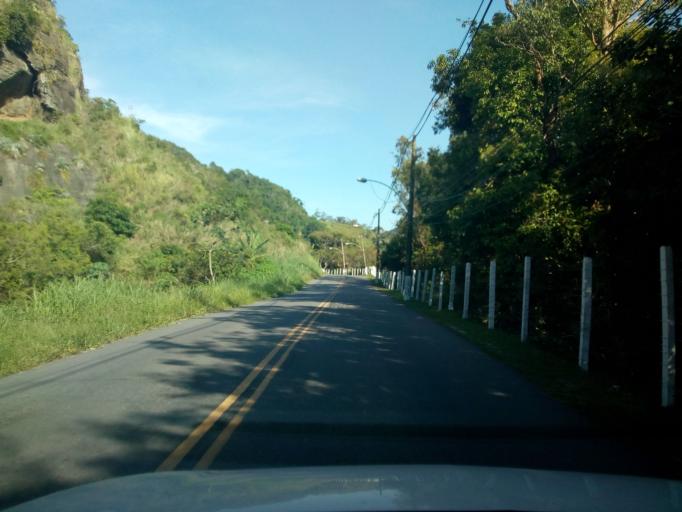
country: BR
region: Rio de Janeiro
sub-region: Nilopolis
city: Nilopolis
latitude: -23.0311
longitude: -43.4959
